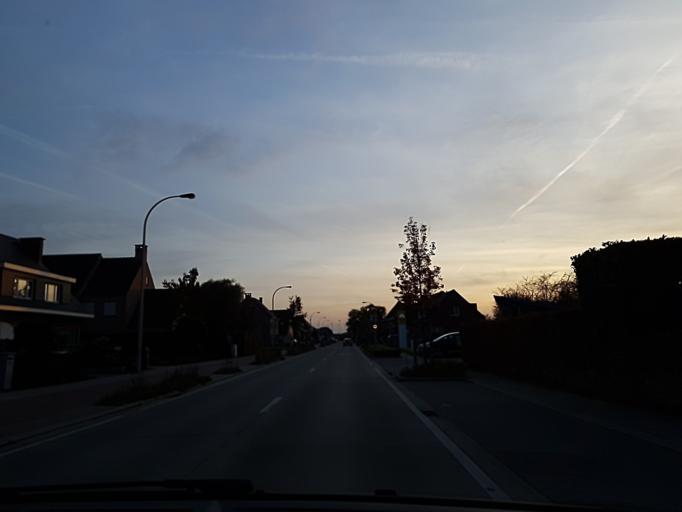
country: BE
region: Flanders
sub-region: Provincie Antwerpen
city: Ranst
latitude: 51.1860
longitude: 4.5627
